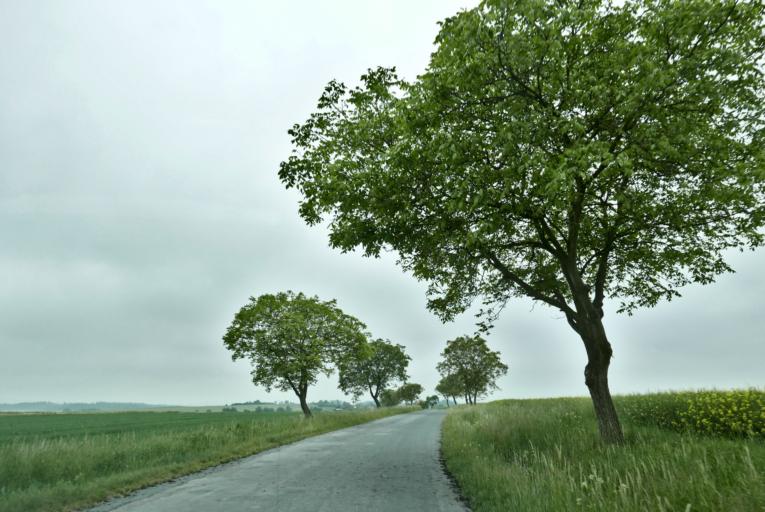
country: CZ
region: Plzensky
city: Zihle
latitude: 50.0335
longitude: 13.3392
